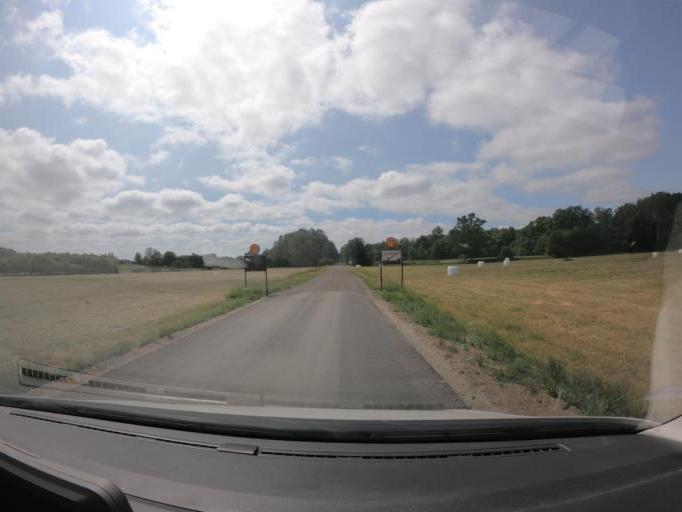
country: SE
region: Skane
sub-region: Hassleholms Kommun
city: Sosdala
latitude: 56.0389
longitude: 13.6711
